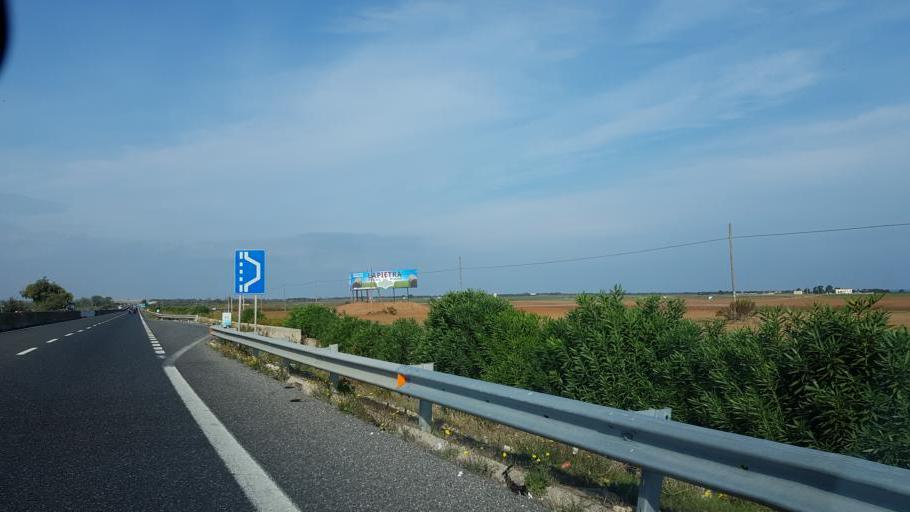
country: IT
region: Apulia
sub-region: Provincia di Brindisi
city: Brindisi
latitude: 40.6713
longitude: 17.8556
